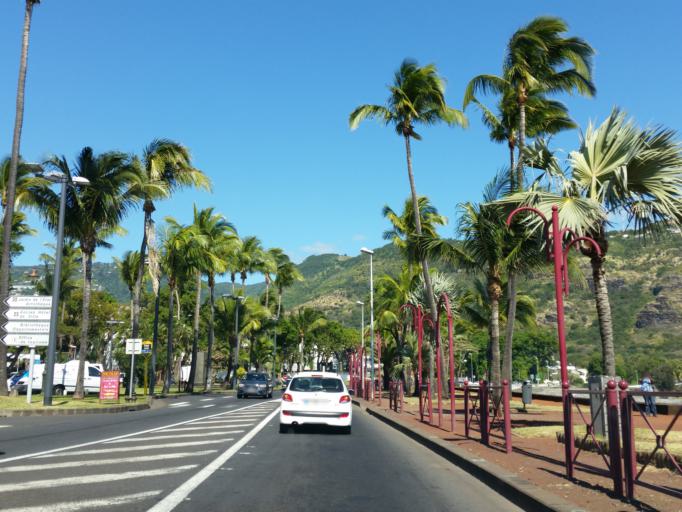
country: RE
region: Reunion
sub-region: Reunion
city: Saint-Denis
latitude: -20.8737
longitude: 55.4467
